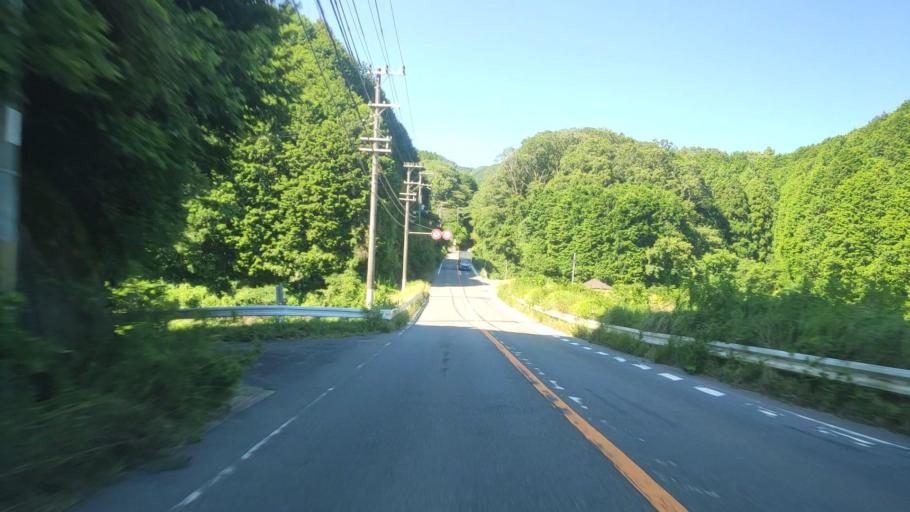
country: JP
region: Nara
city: Haibara-akanedai
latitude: 34.5424
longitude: 135.9575
